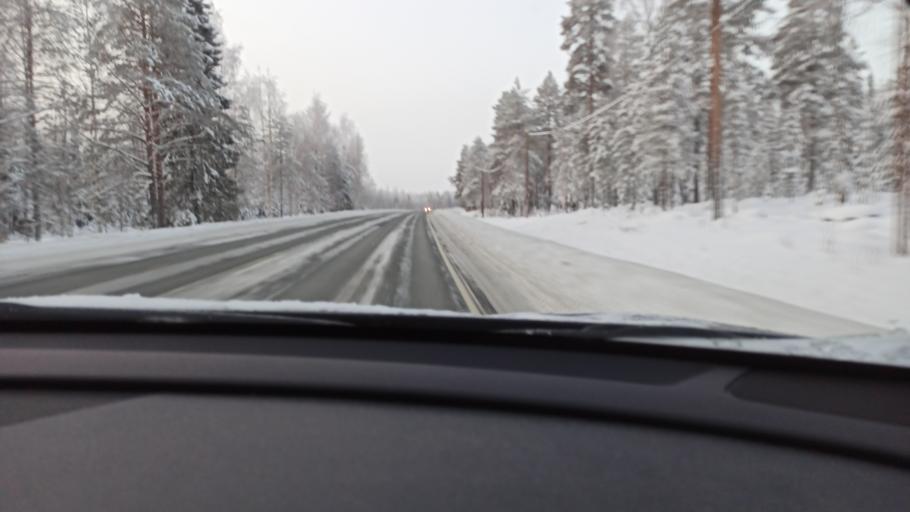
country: FI
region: Lapland
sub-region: Rovaniemi
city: Rovaniemi
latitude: 66.5503
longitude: 25.8864
